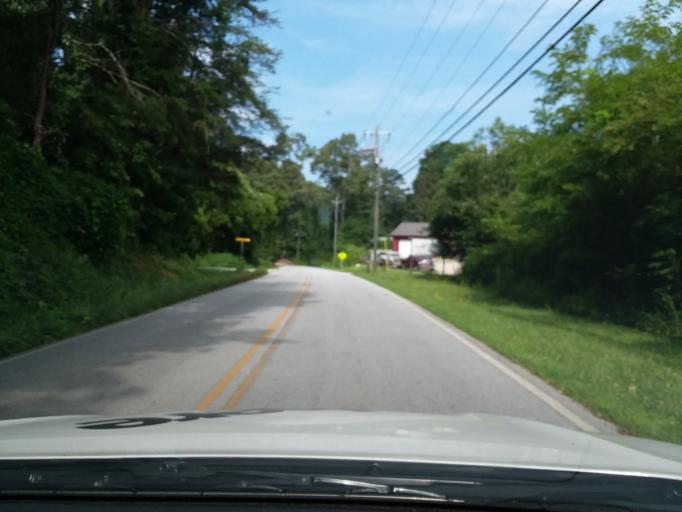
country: US
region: Georgia
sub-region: Rabun County
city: Clayton
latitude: 34.7985
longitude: -83.4218
